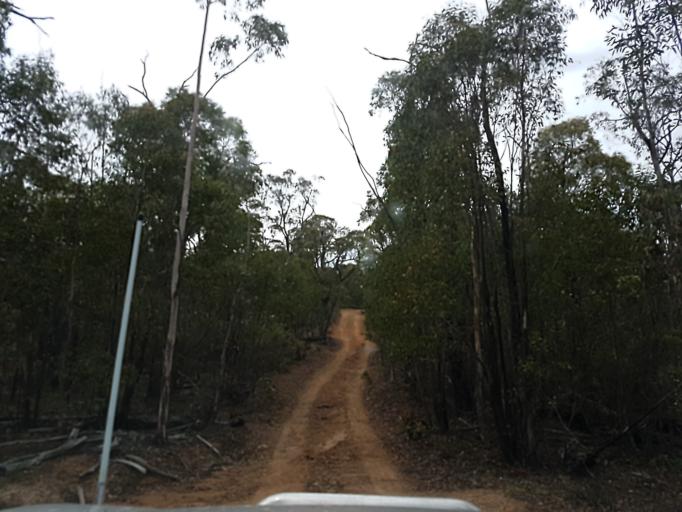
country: AU
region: New South Wales
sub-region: Snowy River
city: Jindabyne
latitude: -36.8622
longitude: 148.2649
